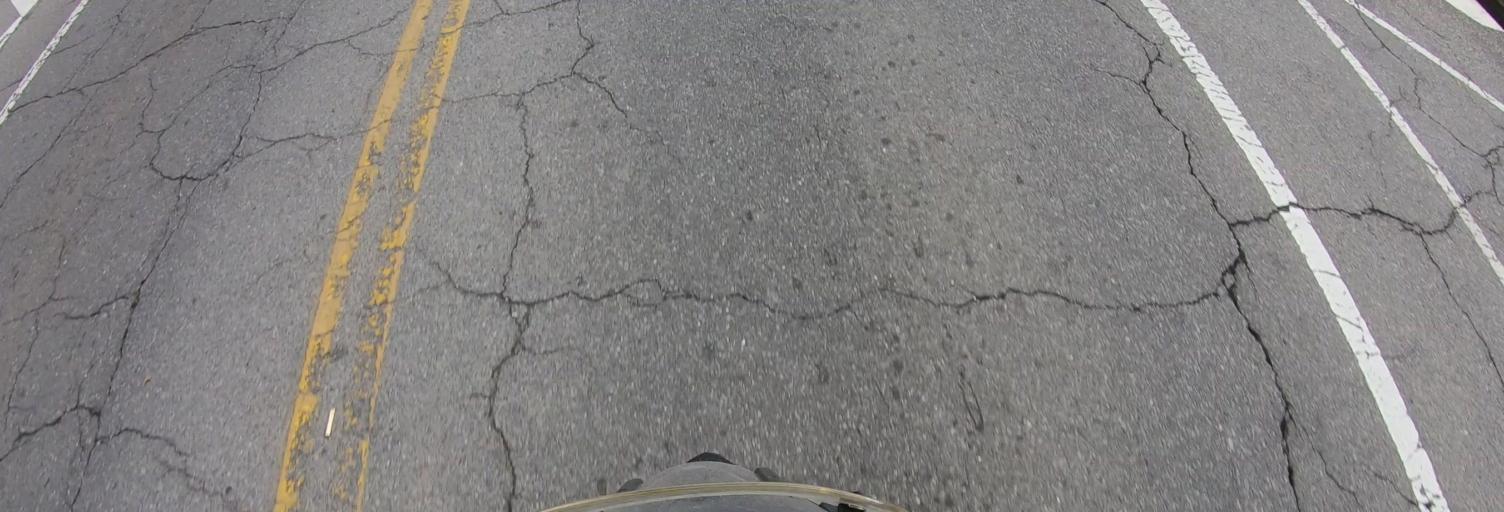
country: US
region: South Carolina
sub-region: York County
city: Rock Hill
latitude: 34.9275
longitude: -81.0225
